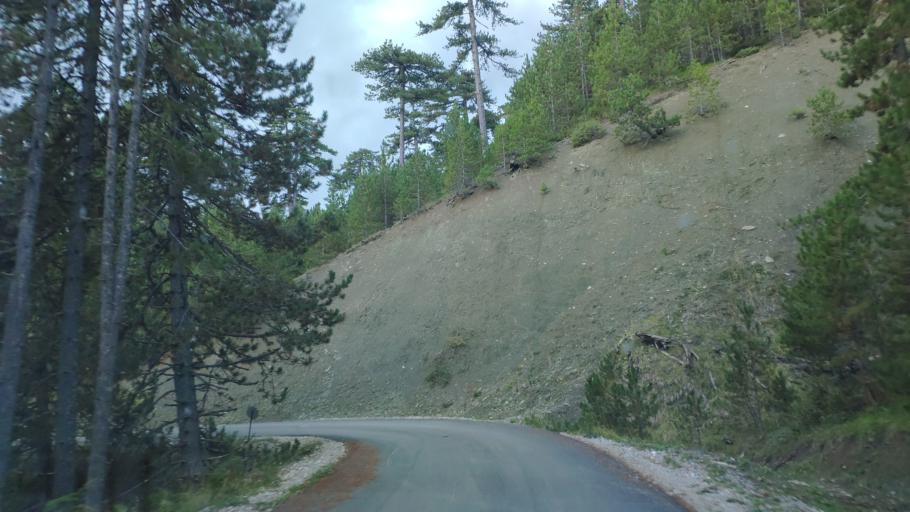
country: AL
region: Korce
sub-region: Rrethi i Kolonjes
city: Erseke
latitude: 40.2941
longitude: 20.8638
